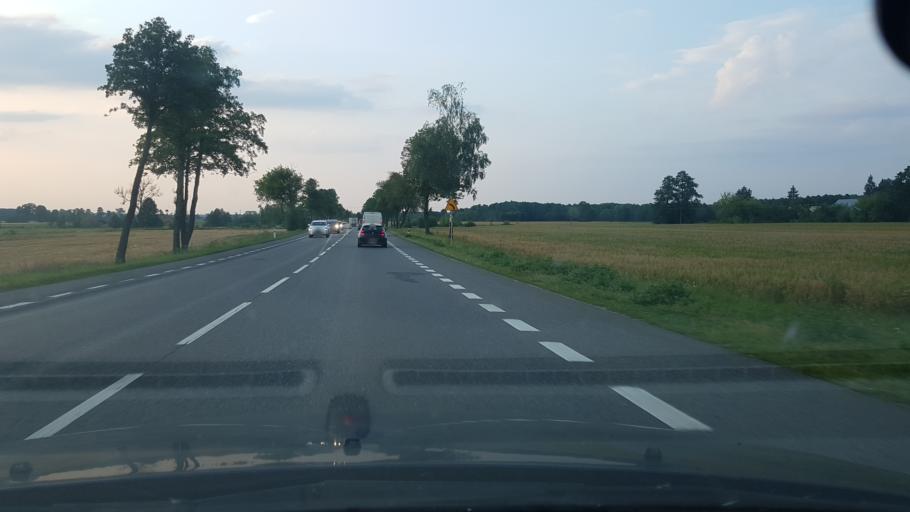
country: PL
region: Masovian Voivodeship
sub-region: Powiat mlawski
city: Strzegowo
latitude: 52.9264
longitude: 20.2860
